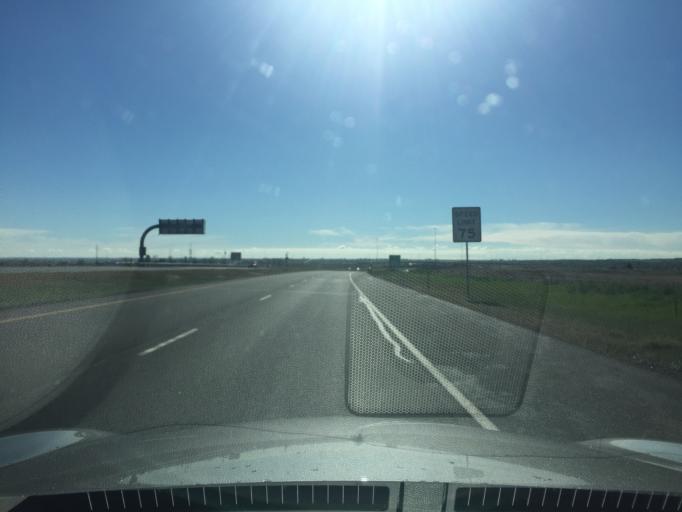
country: US
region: Colorado
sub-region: Boulder County
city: Erie
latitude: 39.9847
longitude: -105.0075
